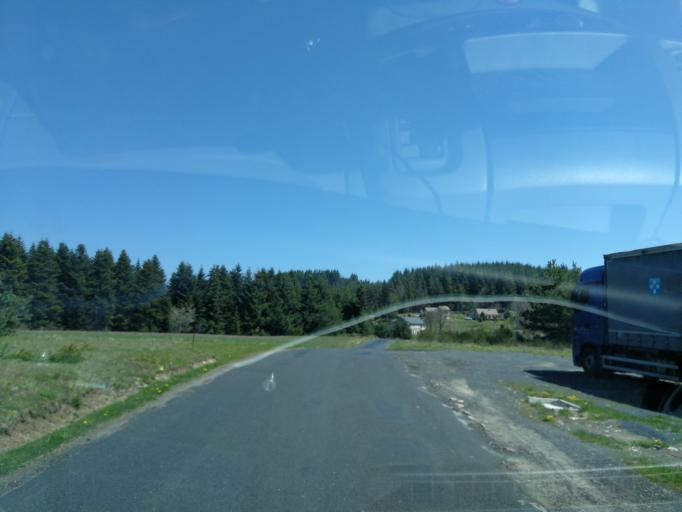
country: FR
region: Rhone-Alpes
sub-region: Departement de l'Ardeche
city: Saint-Agreve
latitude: 44.9760
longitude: 4.4235
